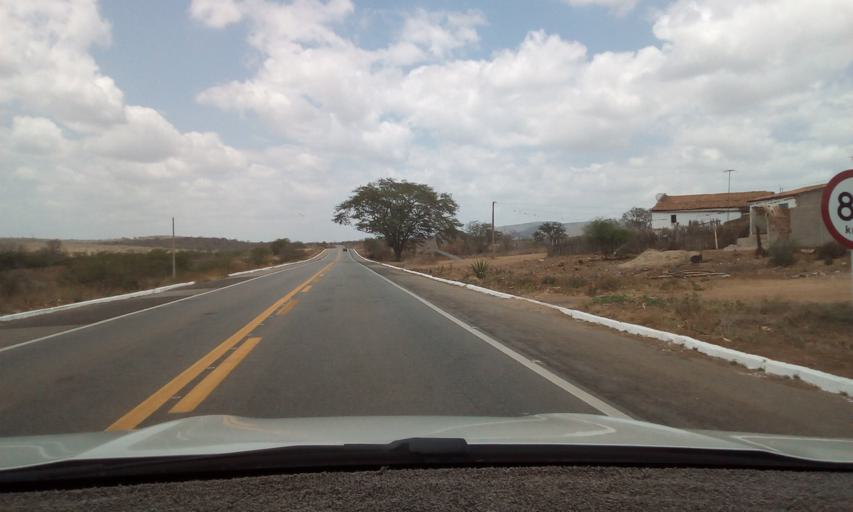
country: BR
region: Pernambuco
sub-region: Taquaritinga Do Norte
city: Taquaritinga do Norte
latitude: -7.7082
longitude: -36.0649
